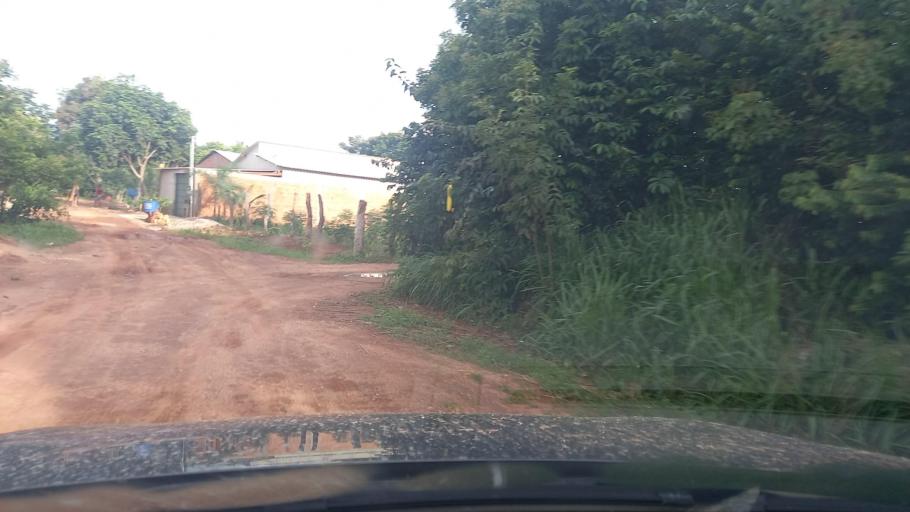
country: BR
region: Goias
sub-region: Cavalcante
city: Cavalcante
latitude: -13.8018
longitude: -47.4450
